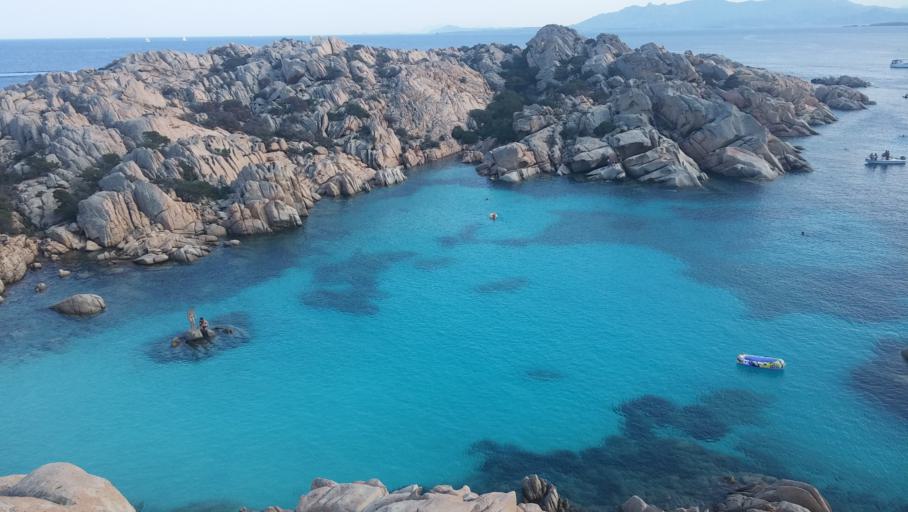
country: IT
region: Sardinia
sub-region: Provincia di Olbia-Tempio
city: La Maddalena
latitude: 41.2182
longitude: 9.4854
